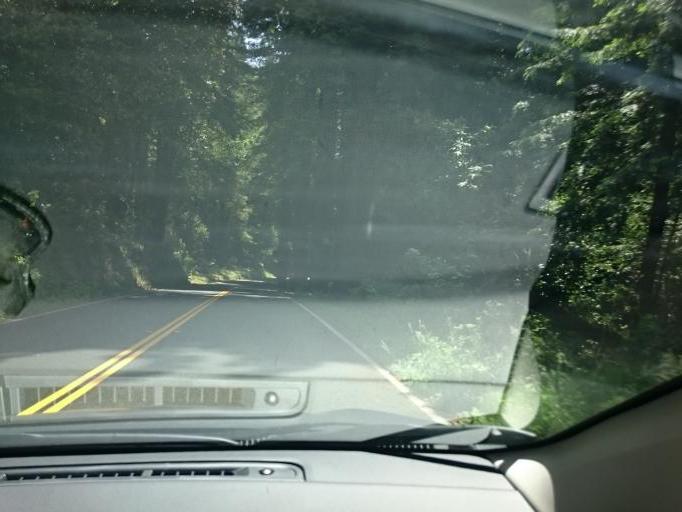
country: US
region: California
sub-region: Mendocino County
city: Fort Bragg
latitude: 39.1788
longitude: -123.6937
